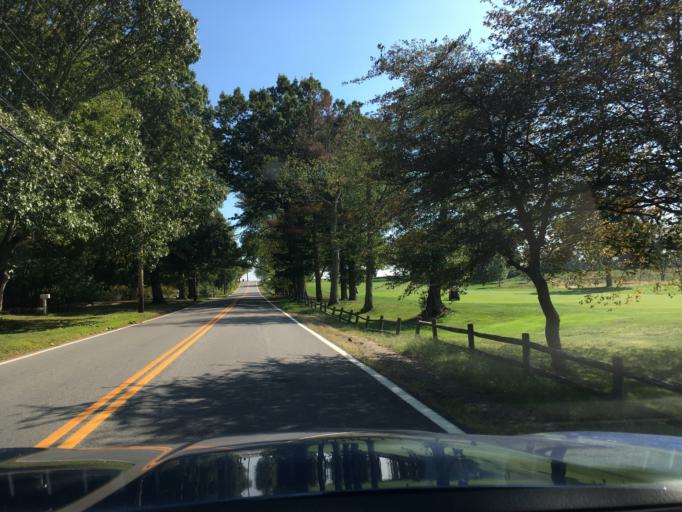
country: US
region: Rhode Island
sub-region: Bristol County
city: Barrington
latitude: 41.7310
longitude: -71.3266
